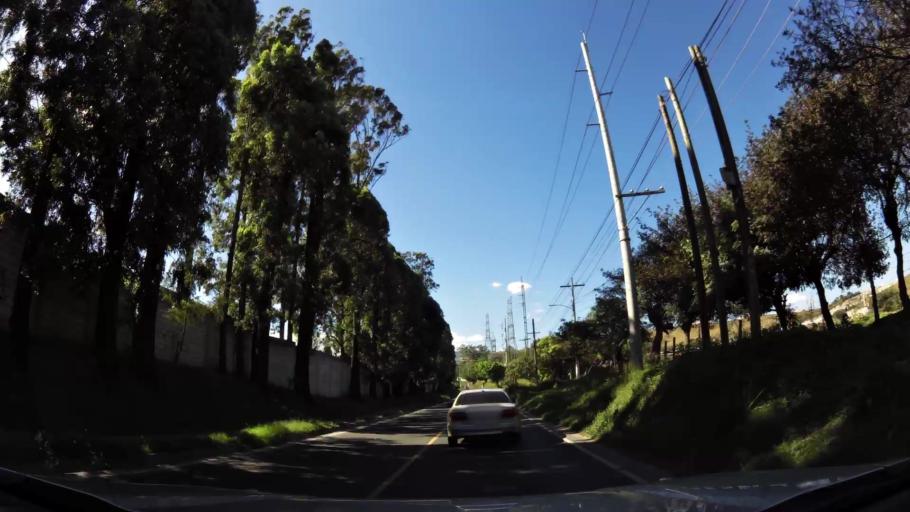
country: GT
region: Guatemala
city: Villa Nueva
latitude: 14.5385
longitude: -90.6073
